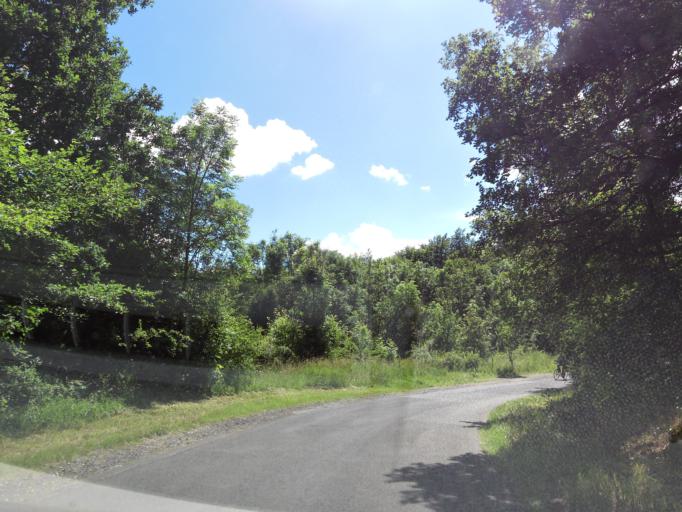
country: DE
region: Lower Saxony
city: Goettingen
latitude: 51.5185
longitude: 9.9796
